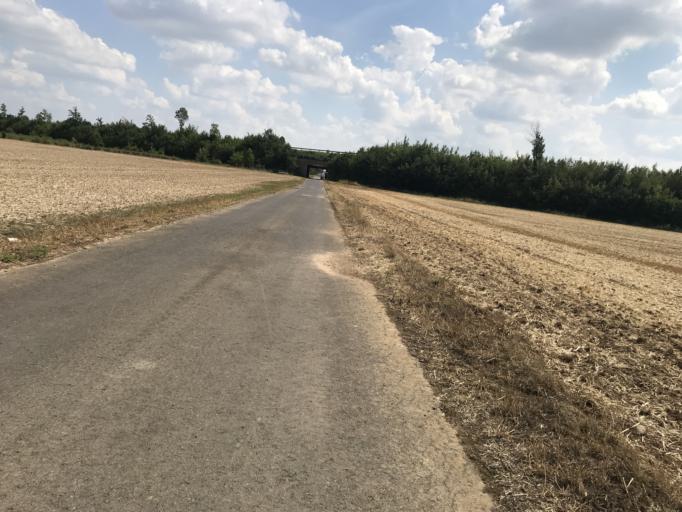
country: DE
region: Hesse
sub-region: Regierungsbezirk Darmstadt
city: Wolfersheim
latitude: 50.4194
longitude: 8.8373
